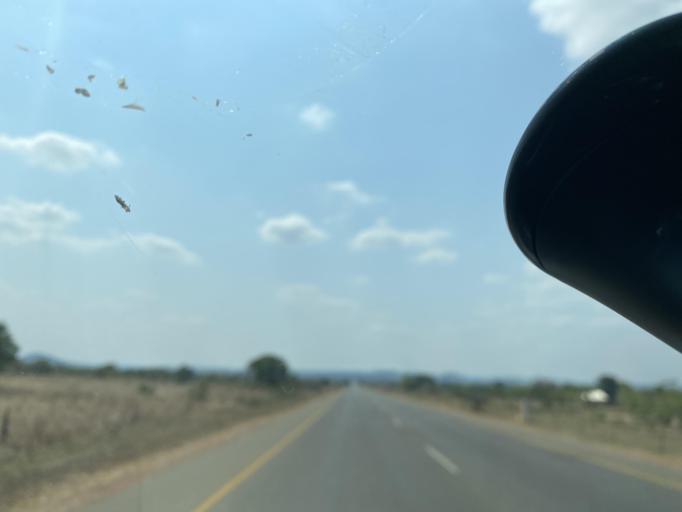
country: ZM
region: Lusaka
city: Chongwe
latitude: -15.5712
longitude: 28.6958
